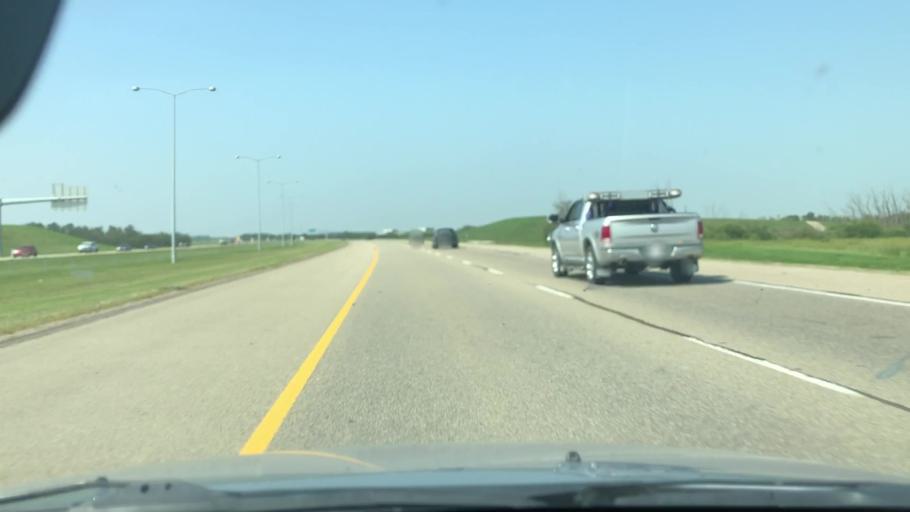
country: CA
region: Alberta
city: Edmonton
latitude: 53.6468
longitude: -113.5141
